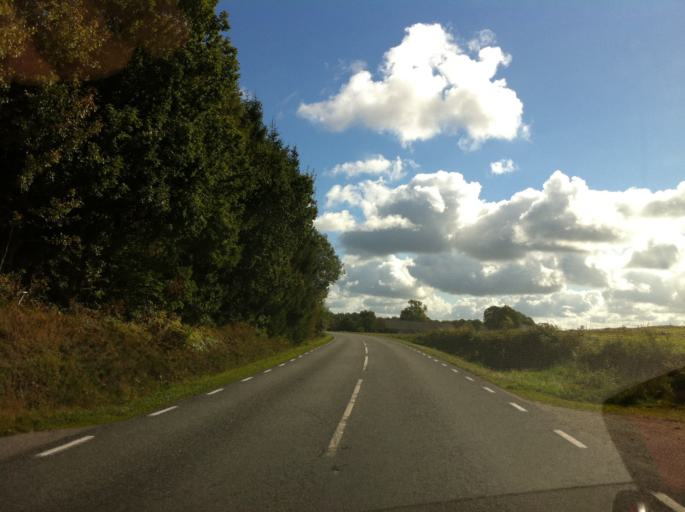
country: SE
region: Skane
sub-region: Kristianstads Kommun
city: Degeberga
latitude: 55.7862
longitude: 13.8696
